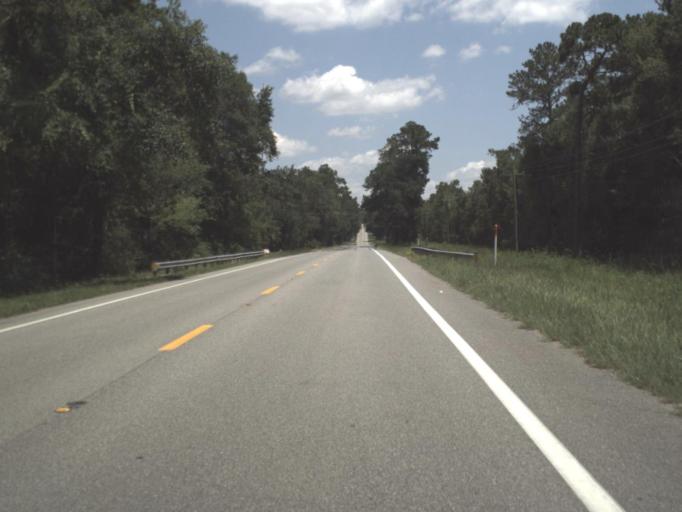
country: US
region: Florida
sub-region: Madison County
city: Madison
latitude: 30.5074
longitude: -83.6328
